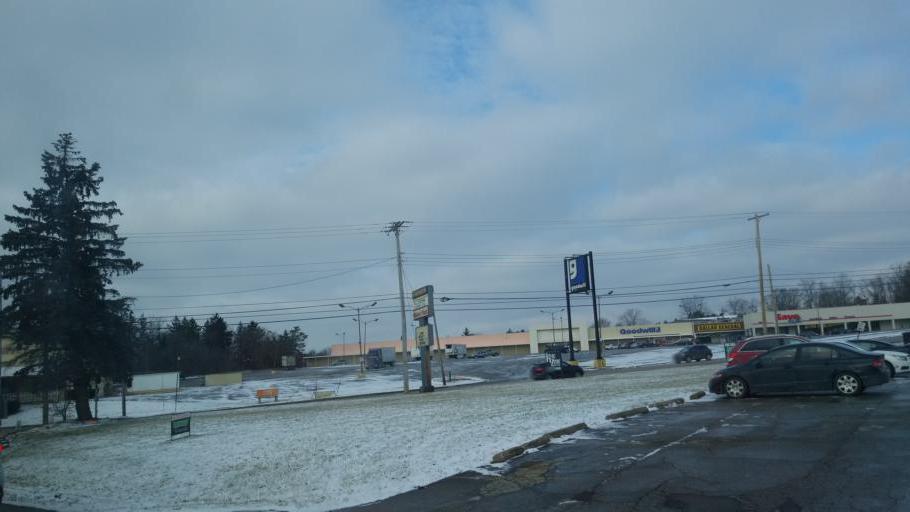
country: US
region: Ohio
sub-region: Richland County
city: Mansfield
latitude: 40.7226
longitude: -82.5417
